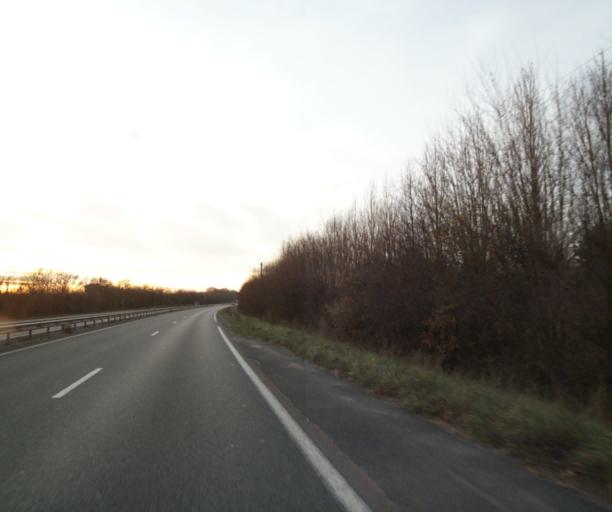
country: FR
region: Poitou-Charentes
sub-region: Departement de la Charente-Maritime
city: Les Gonds
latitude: 45.7305
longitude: -0.6197
